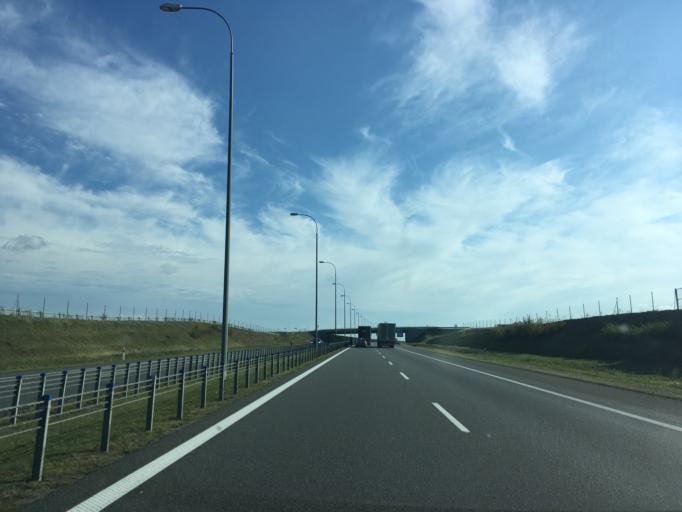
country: PL
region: Kujawsko-Pomorskie
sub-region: Powiat chelminski
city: Lisewo
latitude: 53.3533
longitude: 18.7047
